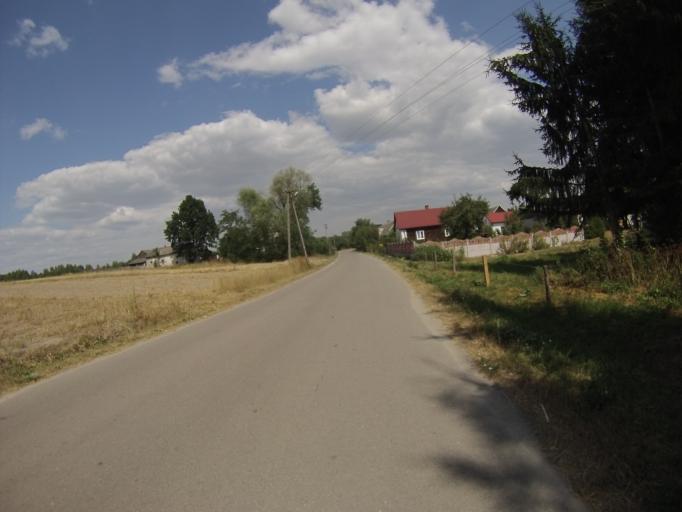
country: PL
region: Swietokrzyskie
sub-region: Powiat kielecki
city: Rakow
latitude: 50.6954
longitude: 21.0895
